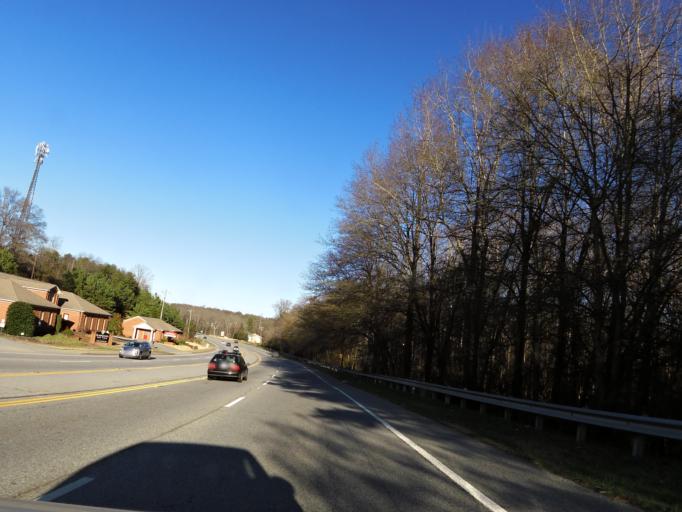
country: US
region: South Carolina
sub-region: Spartanburg County
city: Fairforest
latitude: 34.8910
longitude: -82.0441
